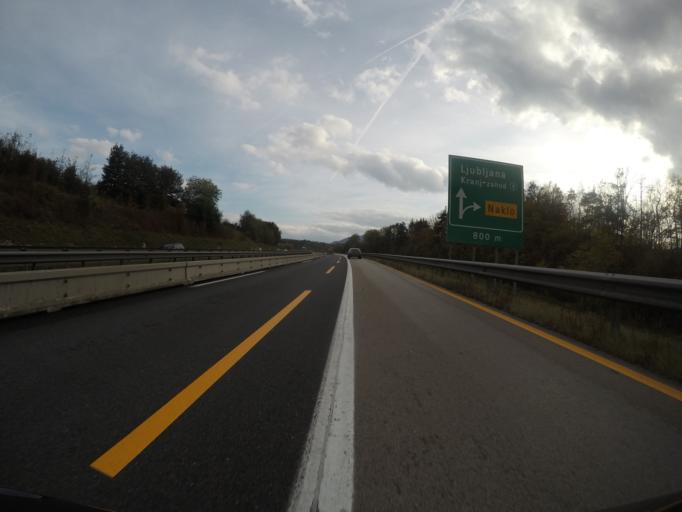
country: SI
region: Naklo
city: Naklo
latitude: 46.2852
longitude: 14.2891
